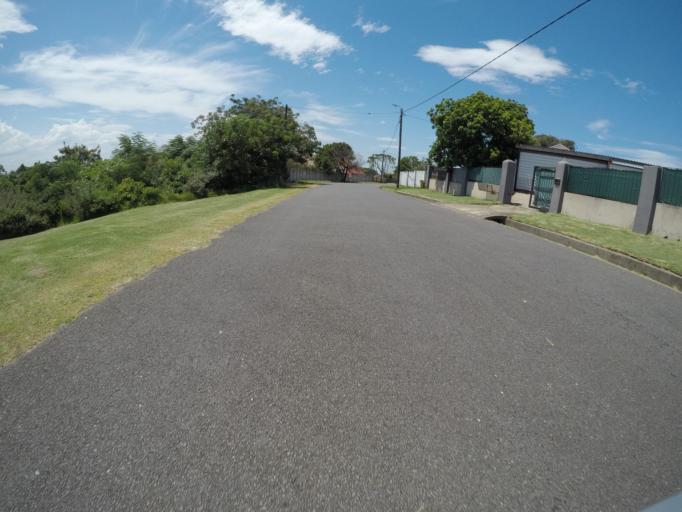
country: ZA
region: Eastern Cape
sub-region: Buffalo City Metropolitan Municipality
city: East London
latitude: -33.0322
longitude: 27.8588
